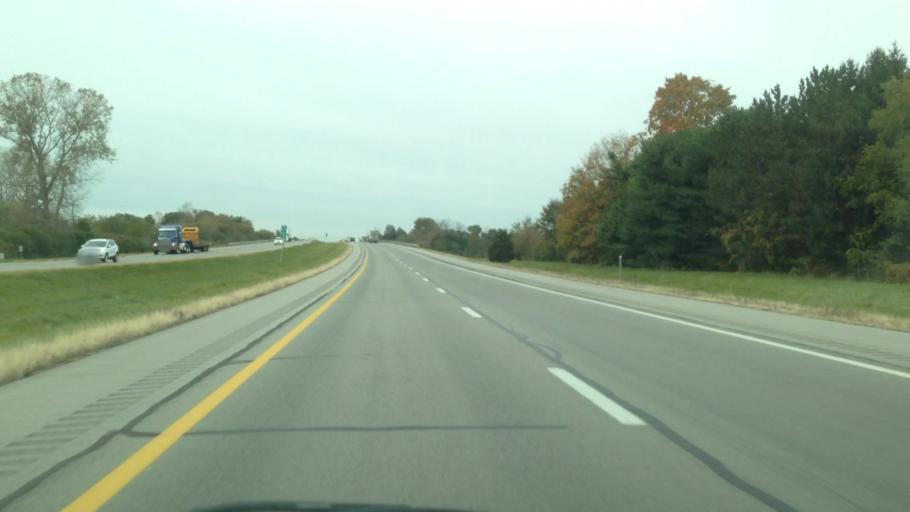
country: US
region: Ohio
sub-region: Lucas County
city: Holland
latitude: 41.5920
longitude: -83.7260
